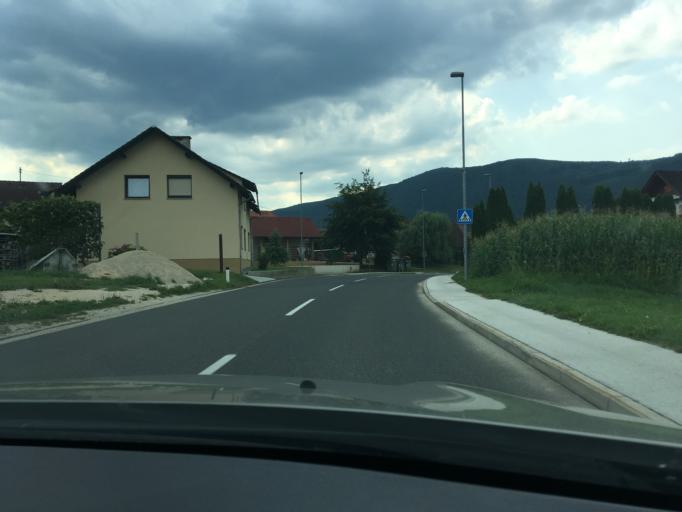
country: SI
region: Straza
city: Straza
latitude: 45.7838
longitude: 15.0952
